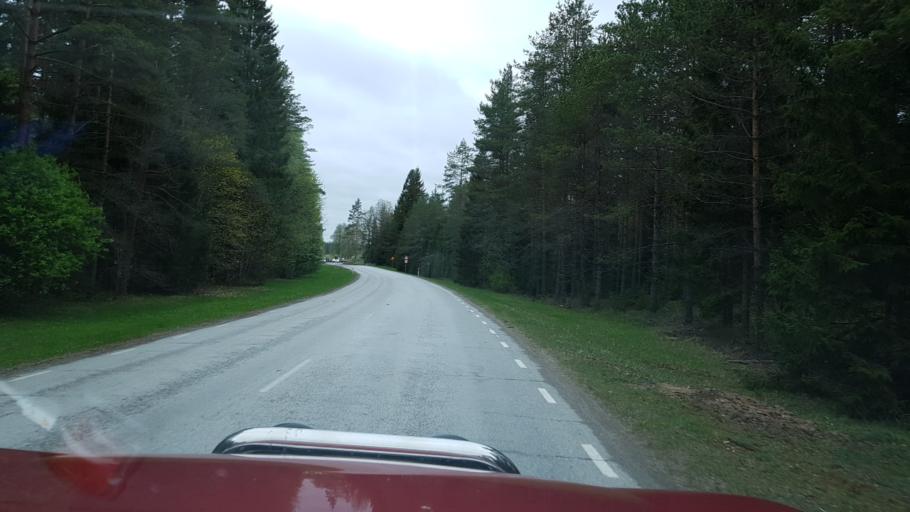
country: EE
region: Vorumaa
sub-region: Voru linn
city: Voru
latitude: 57.8710
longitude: 26.8150
